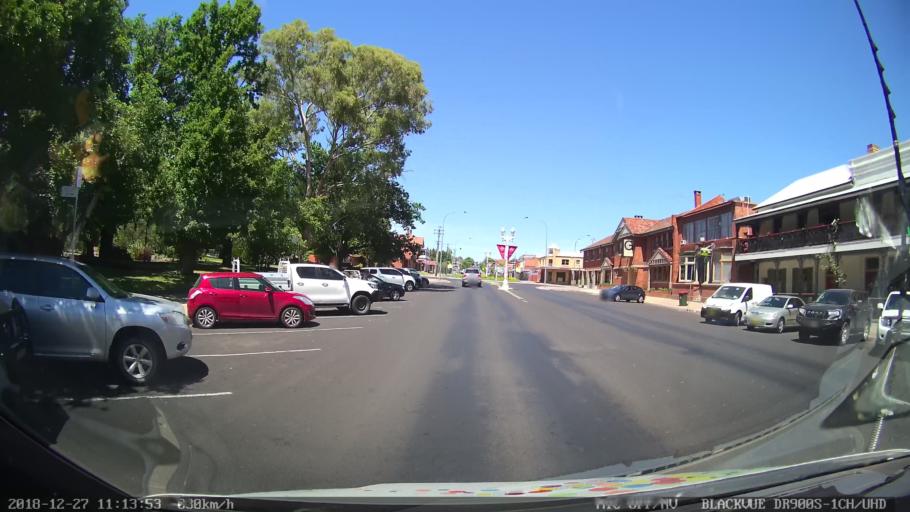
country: AU
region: New South Wales
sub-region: Bathurst Regional
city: Bathurst
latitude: -33.4180
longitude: 149.5769
